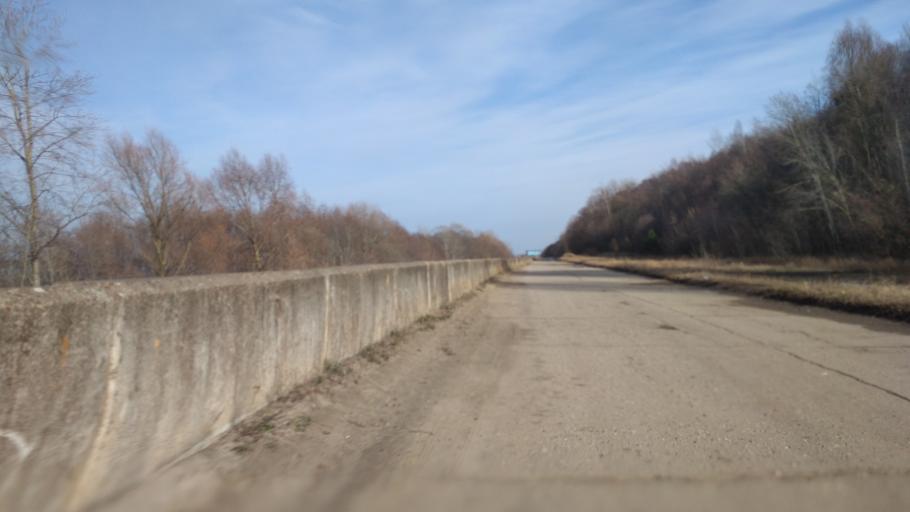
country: RU
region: Chuvashia
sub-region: Cheboksarskiy Rayon
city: Cheboksary
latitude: 56.1461
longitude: 47.3104
